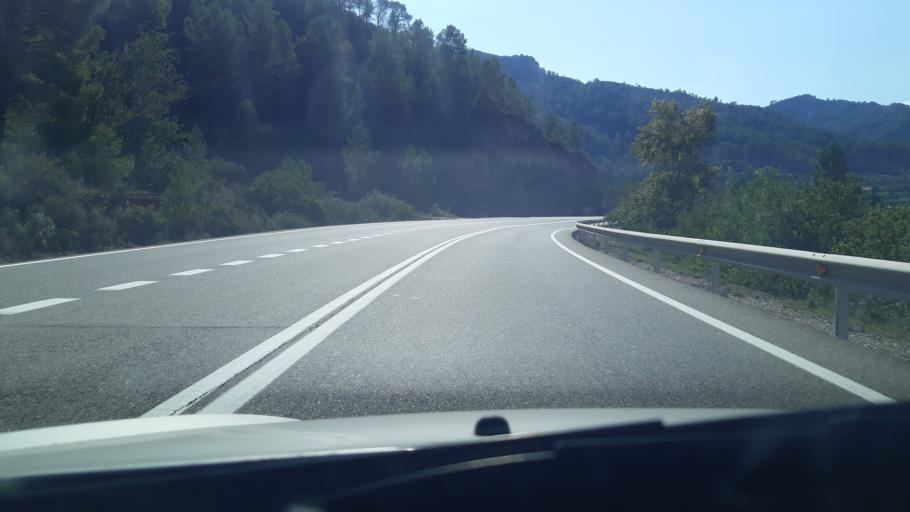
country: ES
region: Catalonia
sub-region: Provincia de Tarragona
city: Benifallet
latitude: 40.9859
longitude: 0.5379
